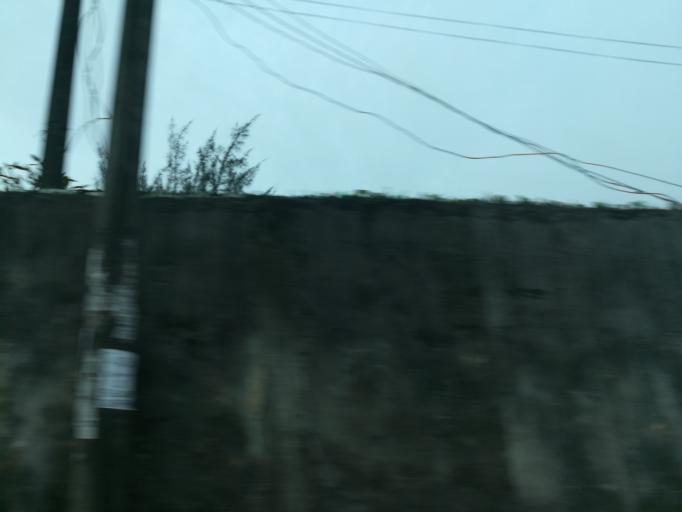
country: NG
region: Rivers
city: Port Harcourt
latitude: 4.8177
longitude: 7.0260
